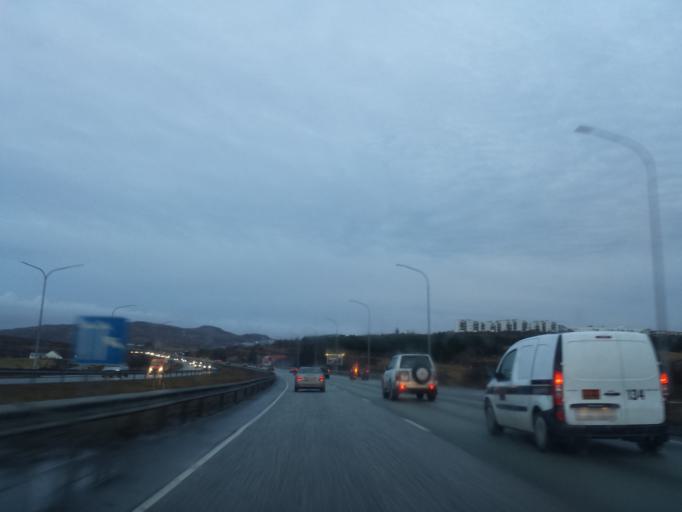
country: IS
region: Capital Region
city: Mosfellsbaer
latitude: 64.1253
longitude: -21.7833
